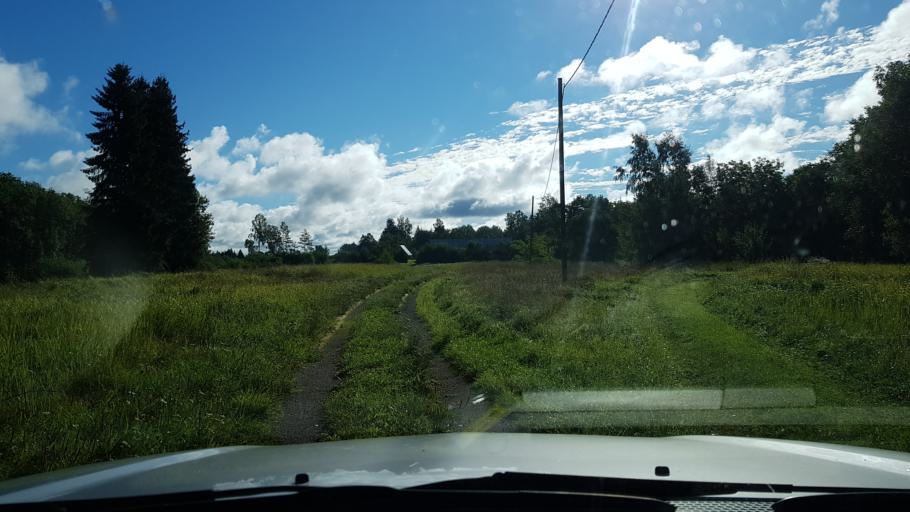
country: EE
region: Harju
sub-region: Rae vald
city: Vaida
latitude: 59.2614
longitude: 25.0283
